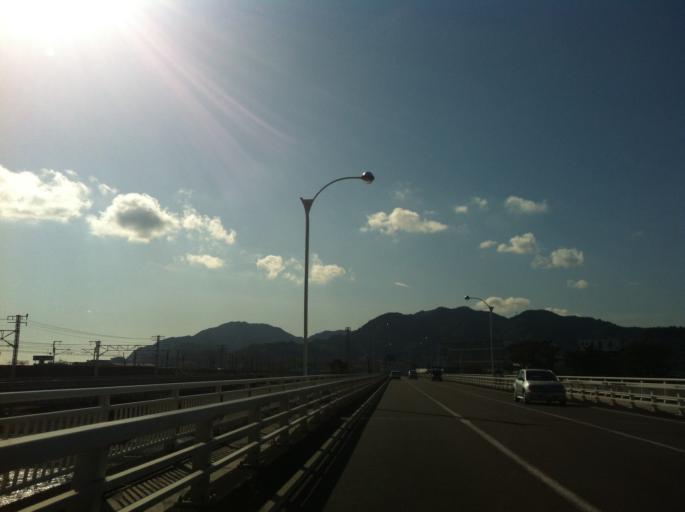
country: JP
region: Shizuoka
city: Shizuoka-shi
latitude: 34.9567
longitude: 138.3703
